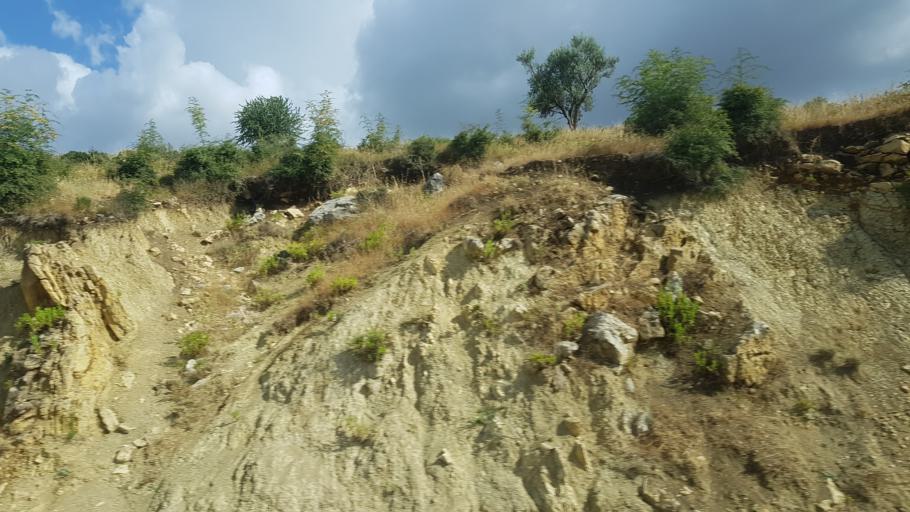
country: AL
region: Vlore
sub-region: Rrethi i Delvines
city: Mesopotam
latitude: 39.9003
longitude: 20.0788
